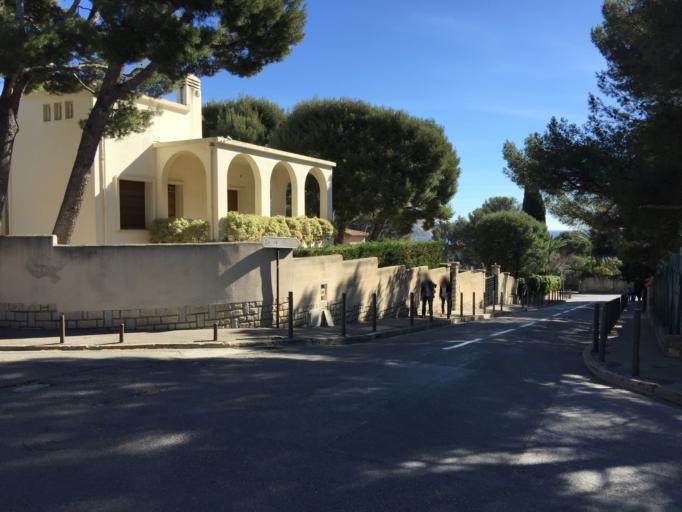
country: FR
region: Provence-Alpes-Cote d'Azur
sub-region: Departement des Bouches-du-Rhone
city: Cassis
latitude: 43.2123
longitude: 5.5263
